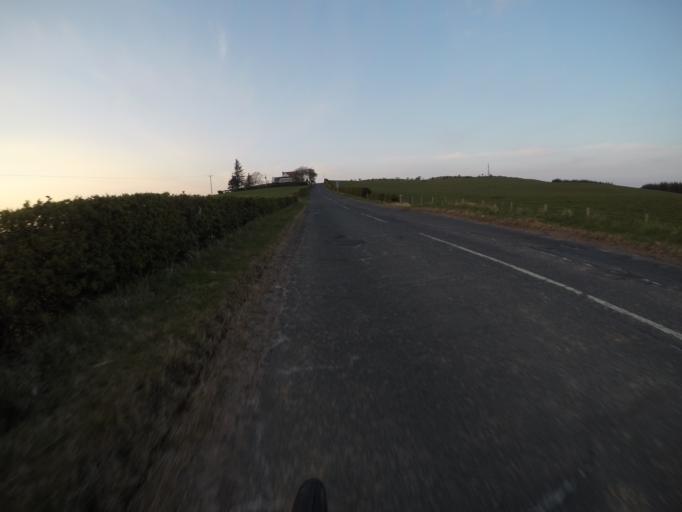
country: GB
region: Scotland
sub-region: South Ayrshire
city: Dundonald
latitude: 55.5525
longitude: -4.6192
